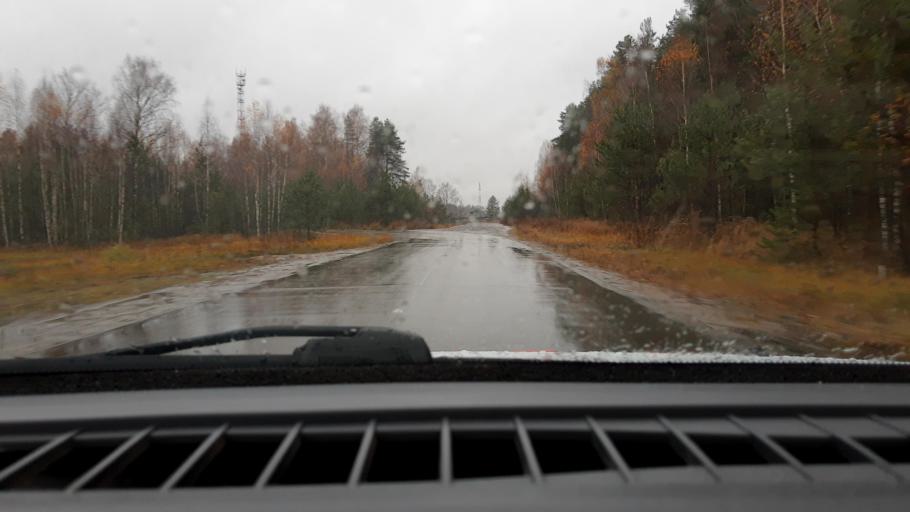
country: RU
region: Nizjnij Novgorod
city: Linda
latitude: 56.6932
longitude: 44.2040
